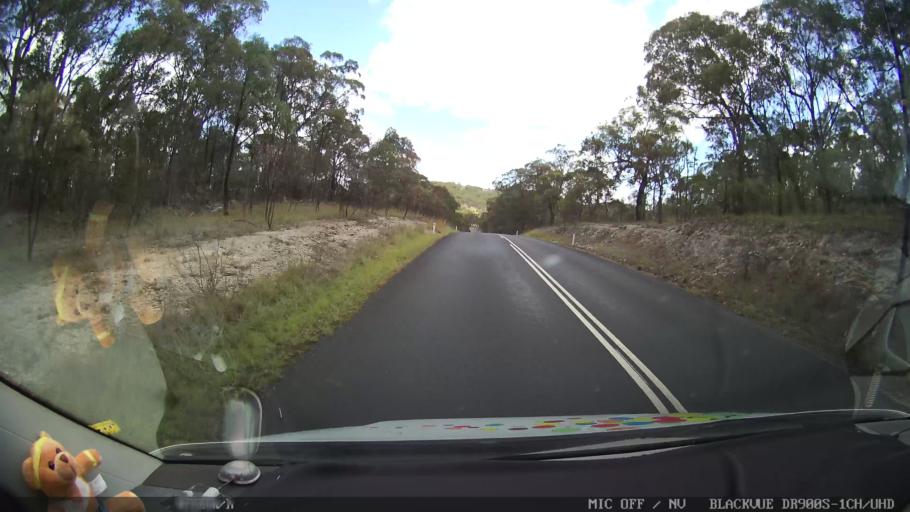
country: AU
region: New South Wales
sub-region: Glen Innes Severn
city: Glen Innes
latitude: -29.5424
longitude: 151.6693
